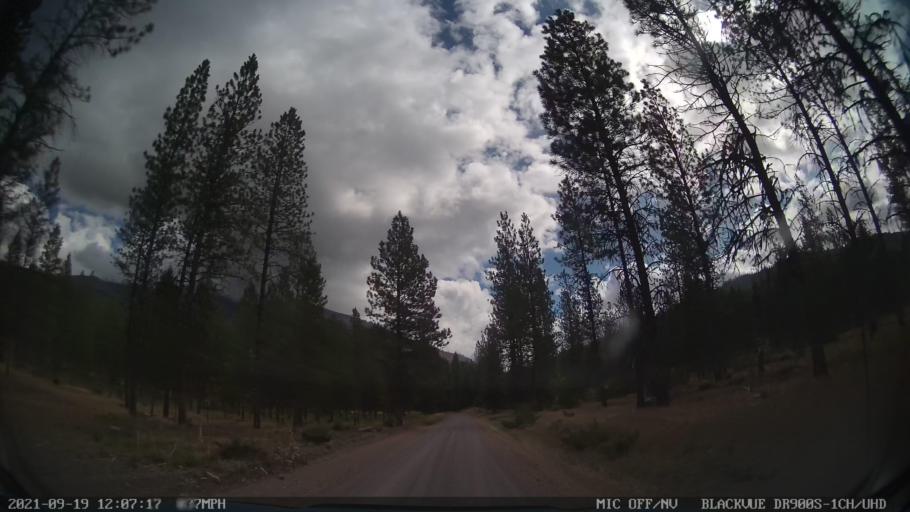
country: US
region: Montana
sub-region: Missoula County
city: Seeley Lake
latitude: 47.1842
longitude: -113.4088
